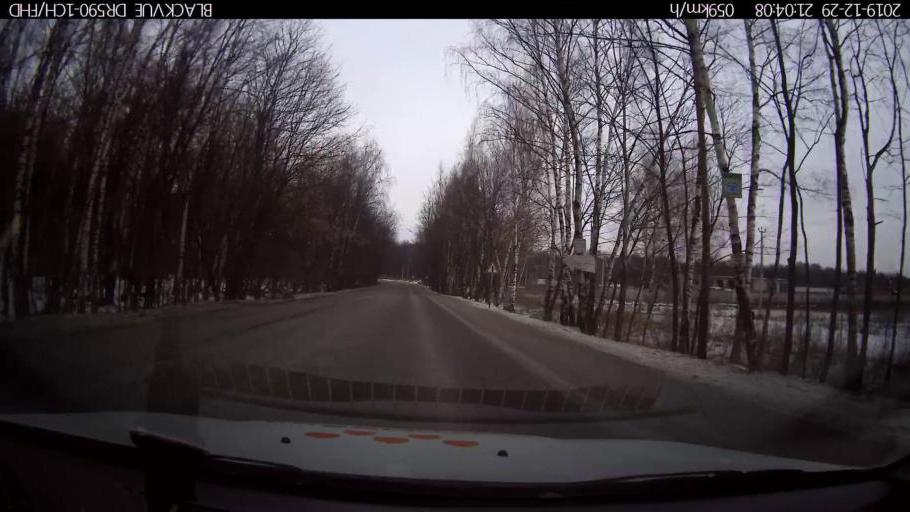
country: RU
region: Nizjnij Novgorod
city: Afonino
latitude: 56.2009
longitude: 44.0036
